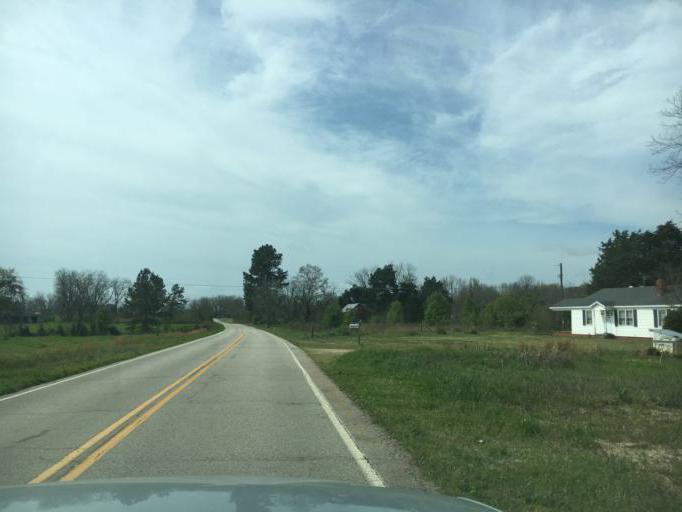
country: US
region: Georgia
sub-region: Hart County
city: Royston
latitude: 34.3182
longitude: -83.0452
